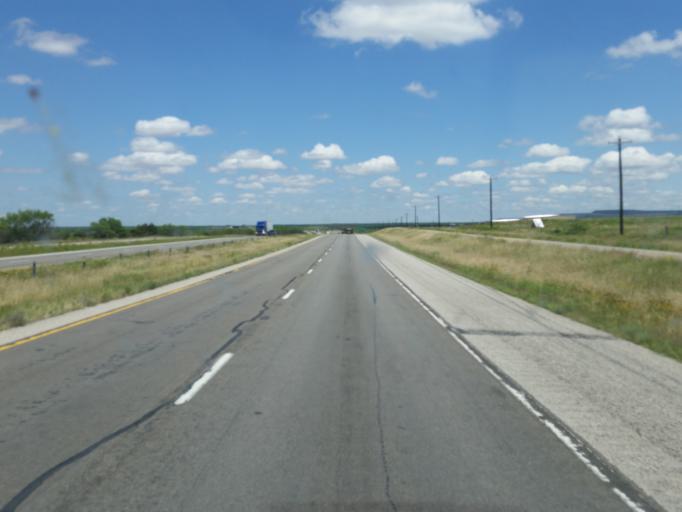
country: US
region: Texas
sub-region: Nolan County
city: Sweetwater
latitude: 32.4946
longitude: -100.2613
